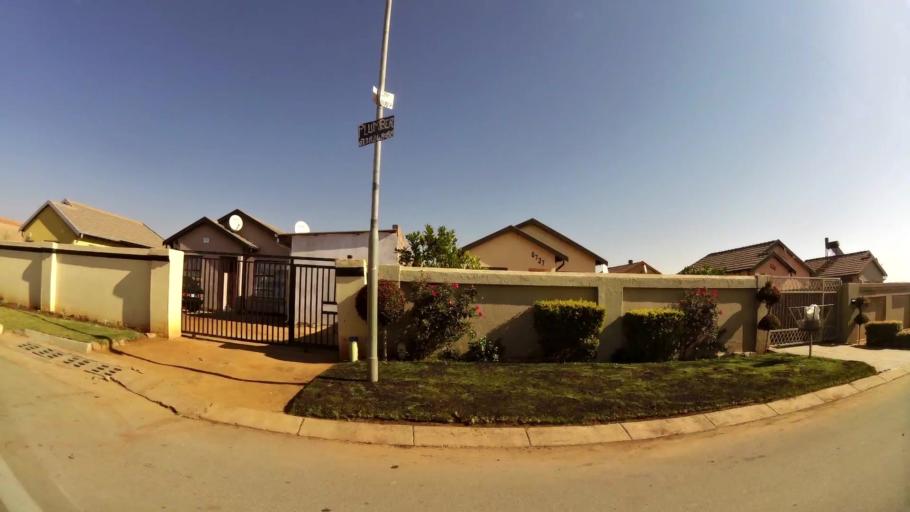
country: ZA
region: Gauteng
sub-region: Ekurhuleni Metropolitan Municipality
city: Tembisa
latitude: -26.0377
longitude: 28.2001
